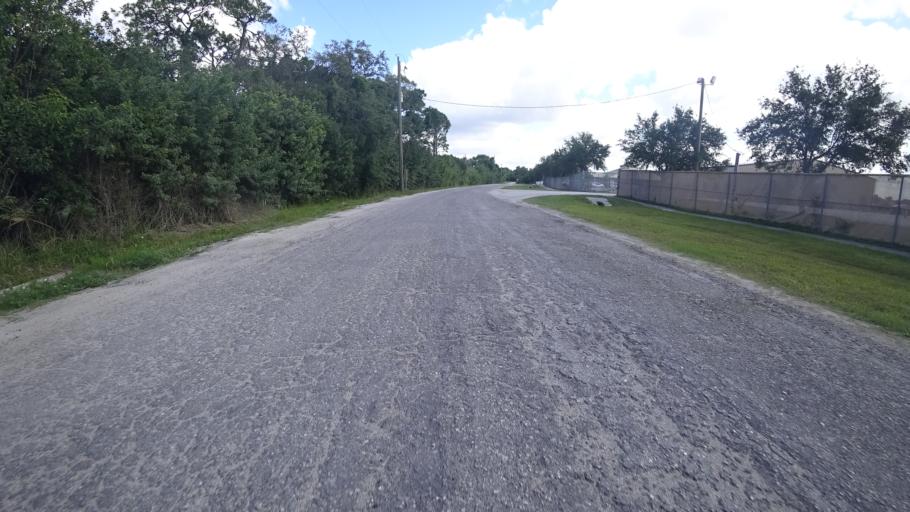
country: US
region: Florida
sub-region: Sarasota County
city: North Sarasota
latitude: 27.4081
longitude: -82.5284
